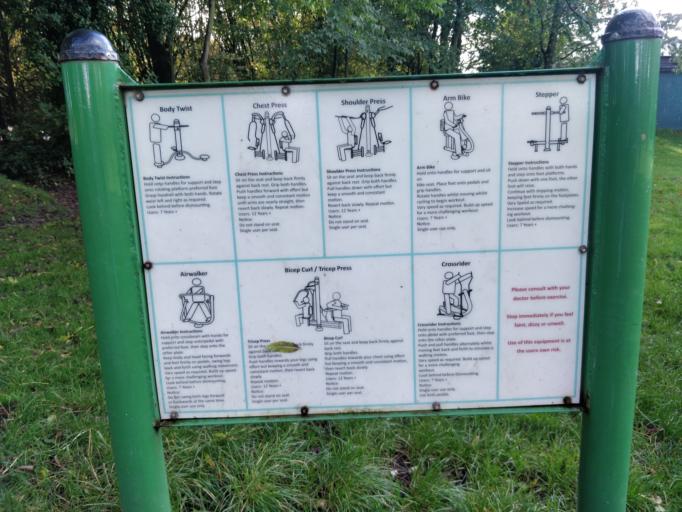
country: GB
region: England
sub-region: Lancashire
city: Banks
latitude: 53.6629
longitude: -2.9568
